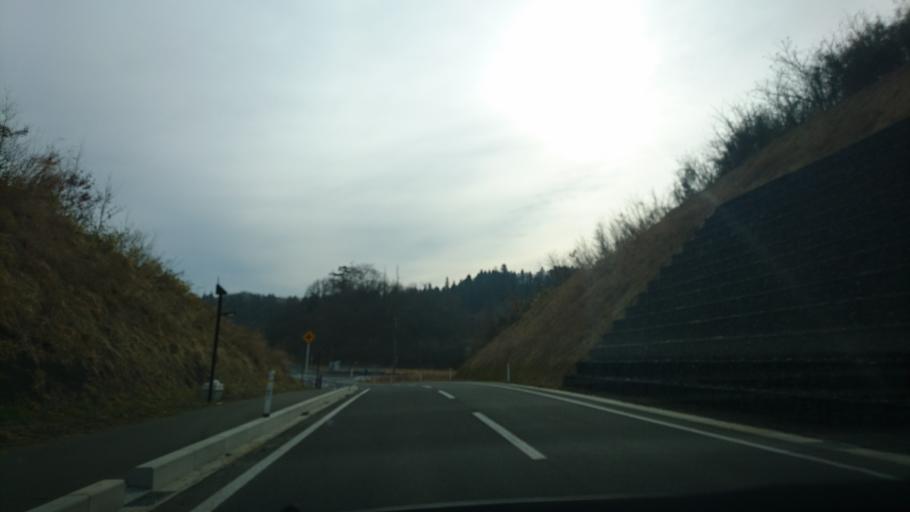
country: JP
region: Iwate
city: Ichinoseki
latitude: 38.9287
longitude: 141.3500
